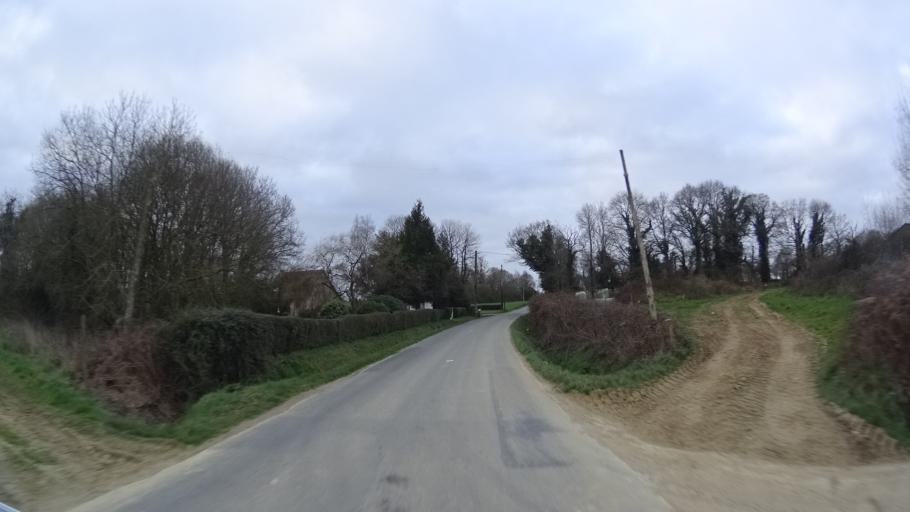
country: FR
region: Brittany
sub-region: Departement d'Ille-et-Vilaine
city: Geveze
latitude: 48.2032
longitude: -1.8296
